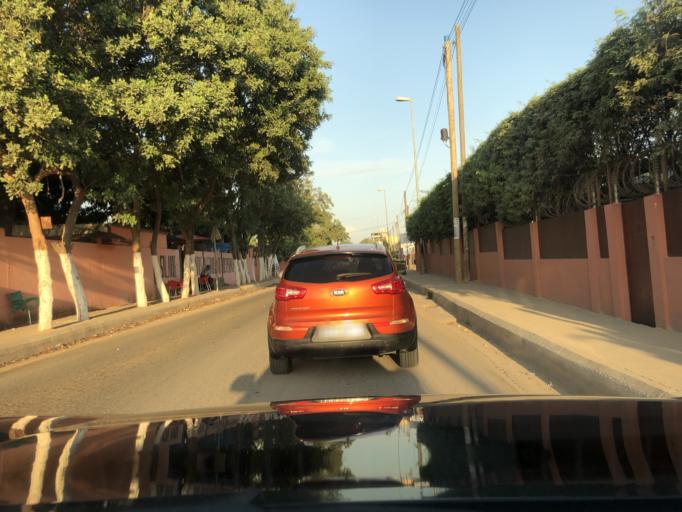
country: AO
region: Luanda
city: Luanda
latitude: -8.9456
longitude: 13.1610
